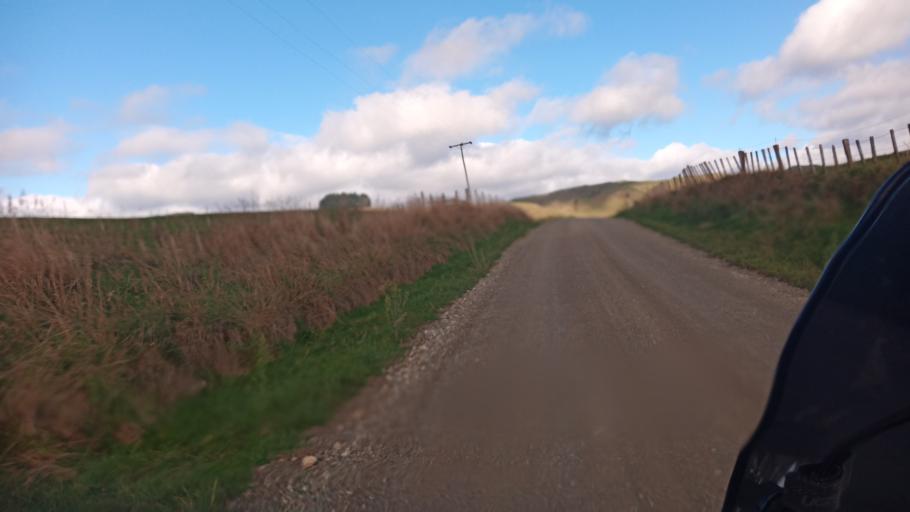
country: NZ
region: Bay of Plenty
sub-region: Opotiki District
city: Opotiki
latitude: -38.4574
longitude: 177.3916
